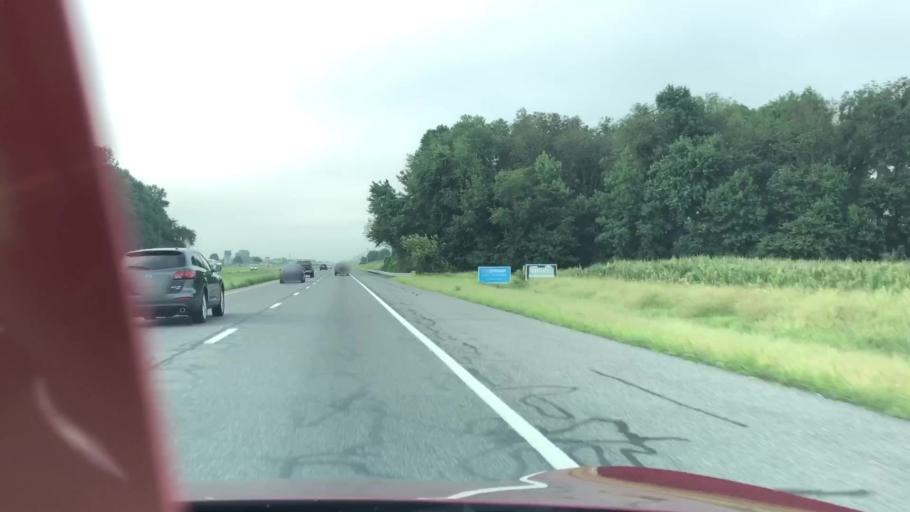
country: US
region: Delaware
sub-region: Sussex County
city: Bridgeville
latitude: 38.7458
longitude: -75.5930
